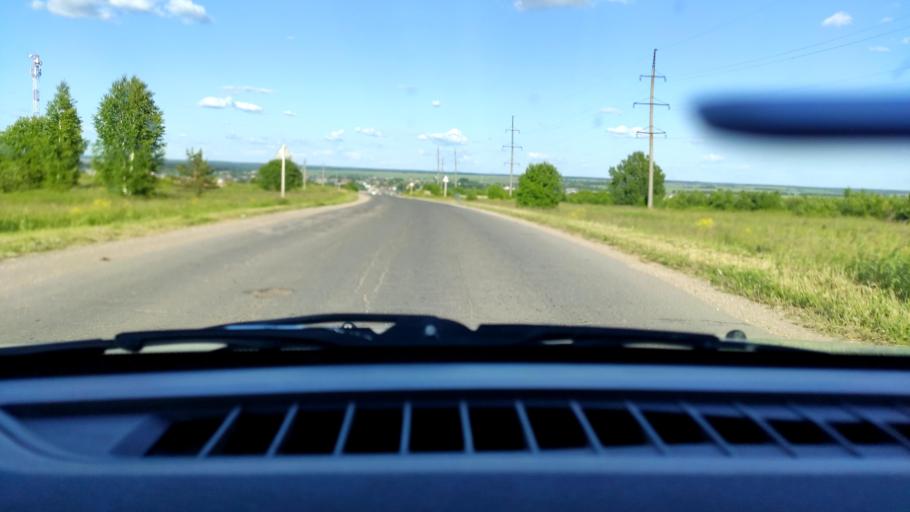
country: RU
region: Perm
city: Orda
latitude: 57.1884
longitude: 56.8784
